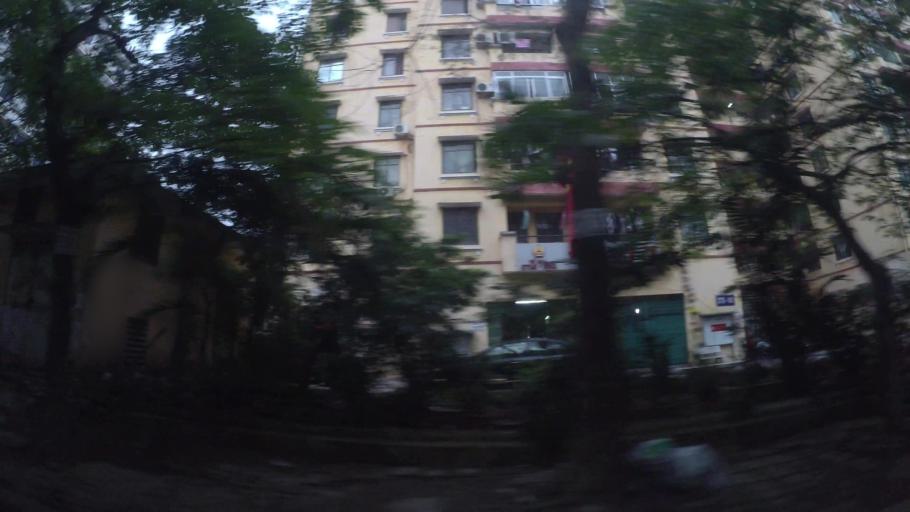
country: VN
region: Ha Noi
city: Thanh Xuan
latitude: 20.9851
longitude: 105.8295
